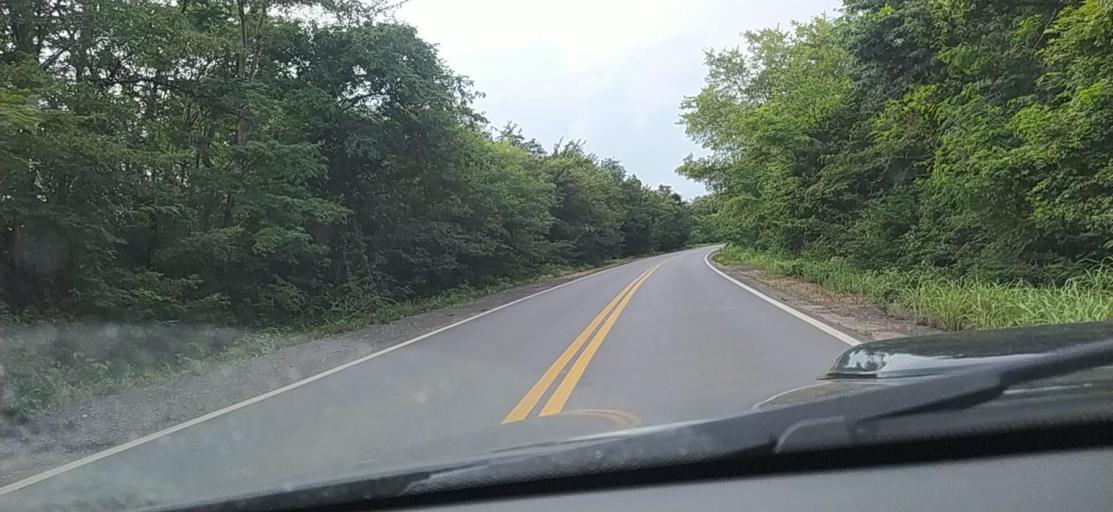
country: BR
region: Minas Gerais
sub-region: Francisco Sa
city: Francisco Sa
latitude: -16.5273
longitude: -43.6797
